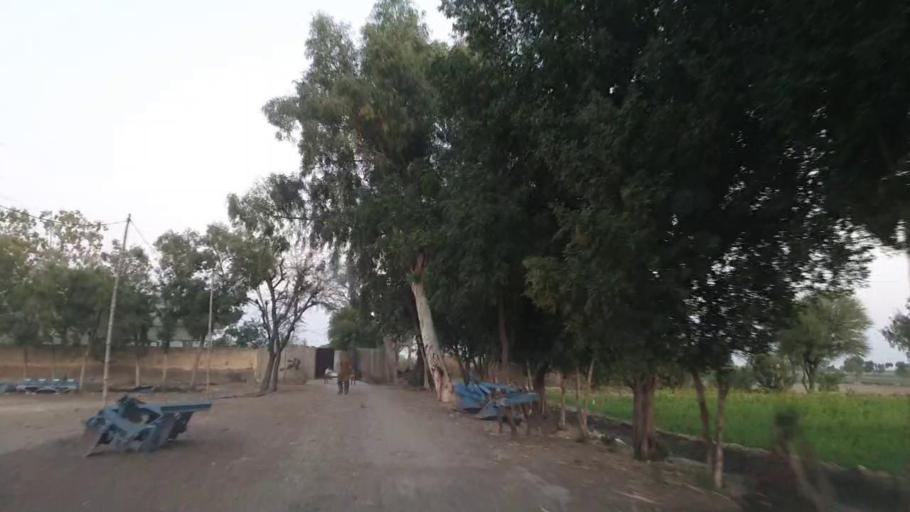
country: PK
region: Sindh
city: Samaro
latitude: 25.3398
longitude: 69.3881
